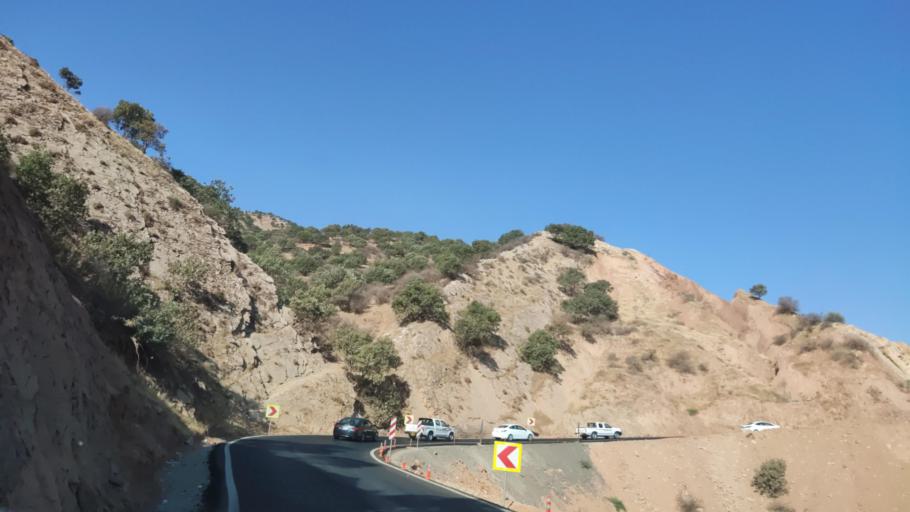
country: IQ
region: Arbil
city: Shaqlawah
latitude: 36.4338
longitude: 44.3017
